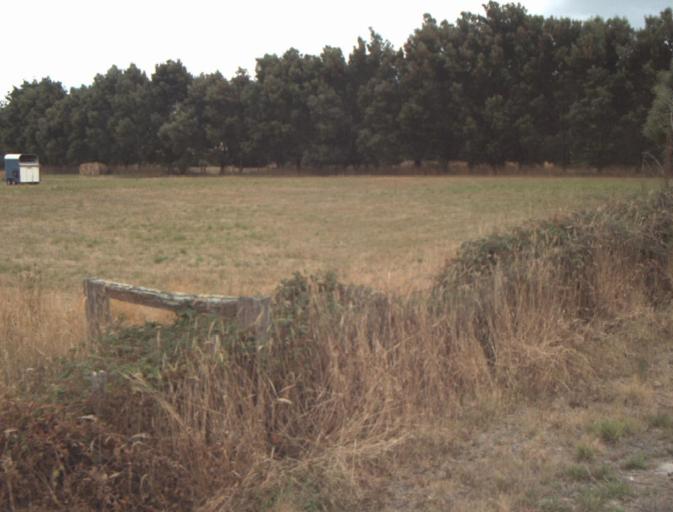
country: AU
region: Tasmania
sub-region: Launceston
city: Mayfield
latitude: -41.2399
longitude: 147.1620
